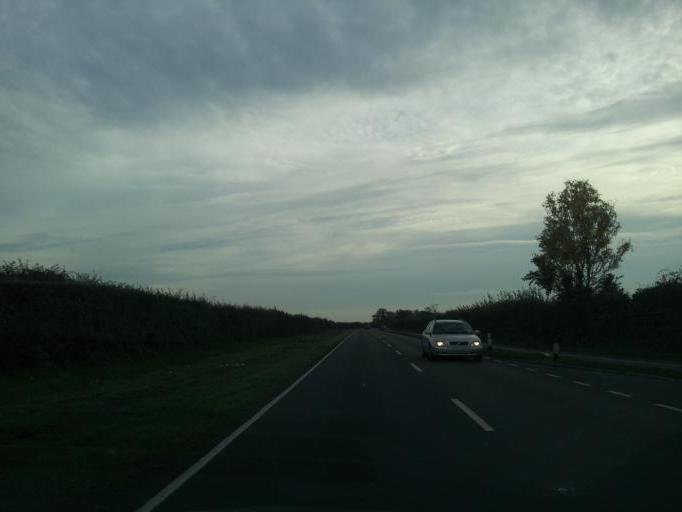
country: GB
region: England
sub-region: Cambridgeshire
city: Duxford
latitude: 52.0925
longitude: 0.1814
